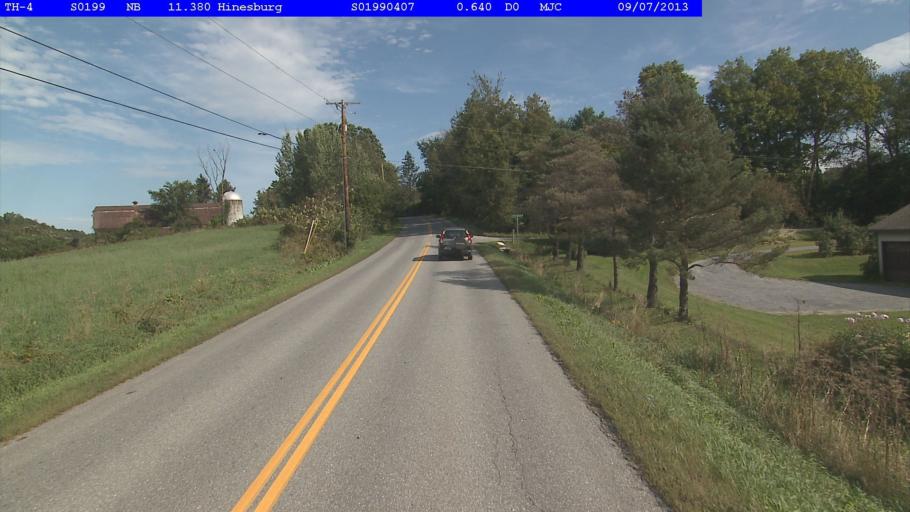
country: US
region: Vermont
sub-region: Chittenden County
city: Hinesburg
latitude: 44.2873
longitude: -73.1072
